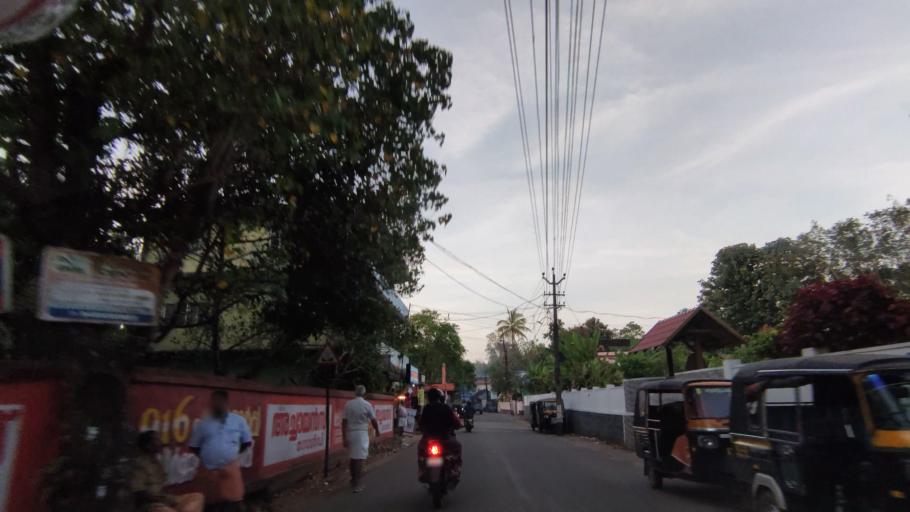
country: IN
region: Kerala
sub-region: Kottayam
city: Kottayam
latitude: 9.6552
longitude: 76.5065
